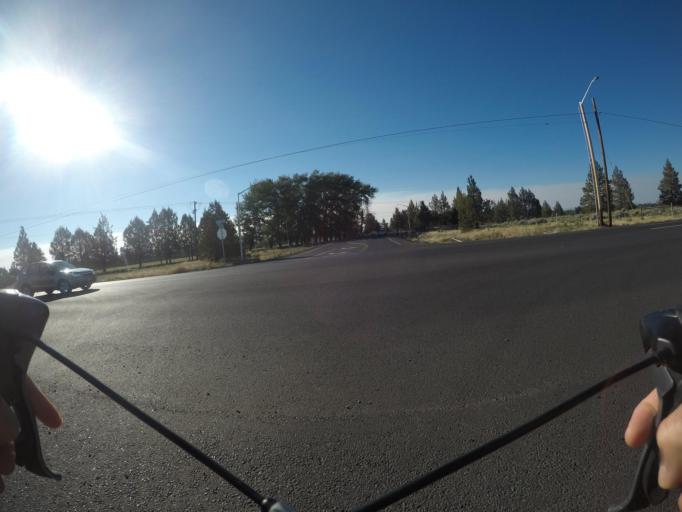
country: US
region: Oregon
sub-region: Deschutes County
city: Redmond
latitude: 44.2101
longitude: -121.2443
